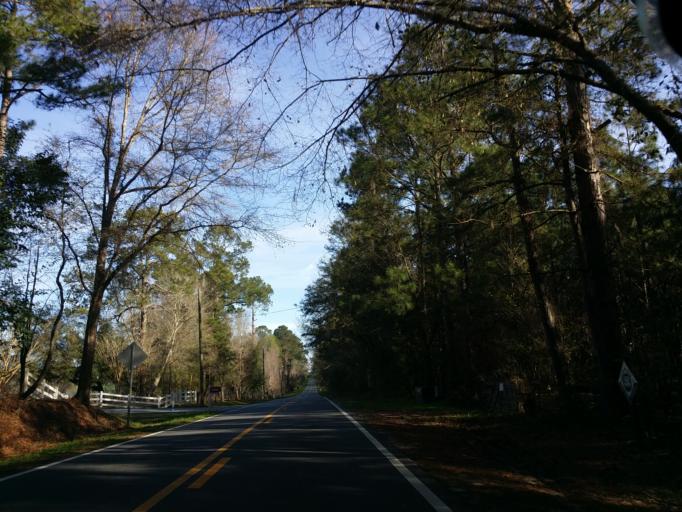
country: US
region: Florida
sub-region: Leon County
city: Woodville
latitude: 30.3993
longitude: -84.1594
